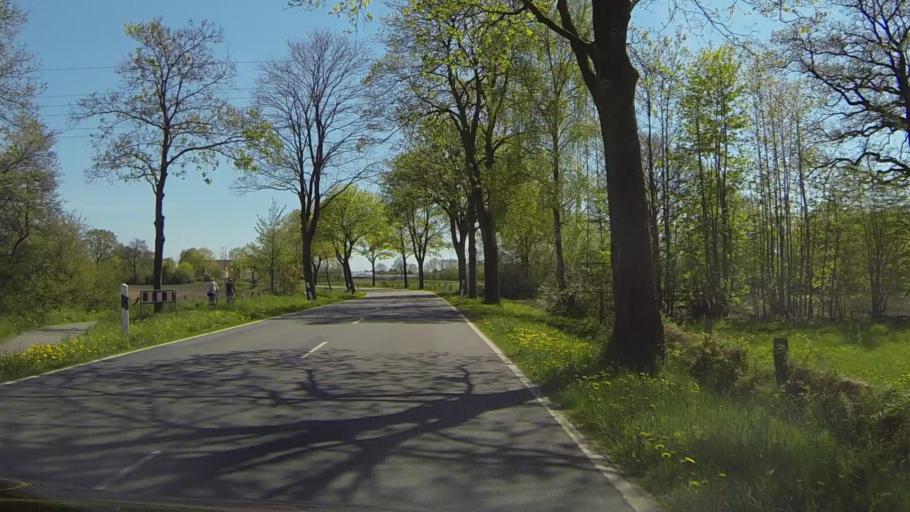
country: DE
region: Schleswig-Holstein
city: Ellerbek
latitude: 53.6522
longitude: 9.8700
